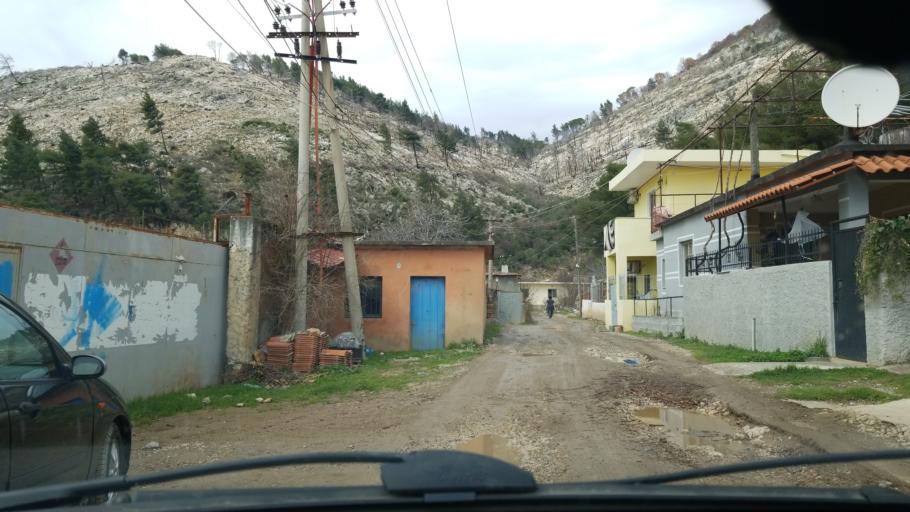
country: AL
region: Lezhe
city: Shengjin
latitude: 41.8159
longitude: 19.5895
